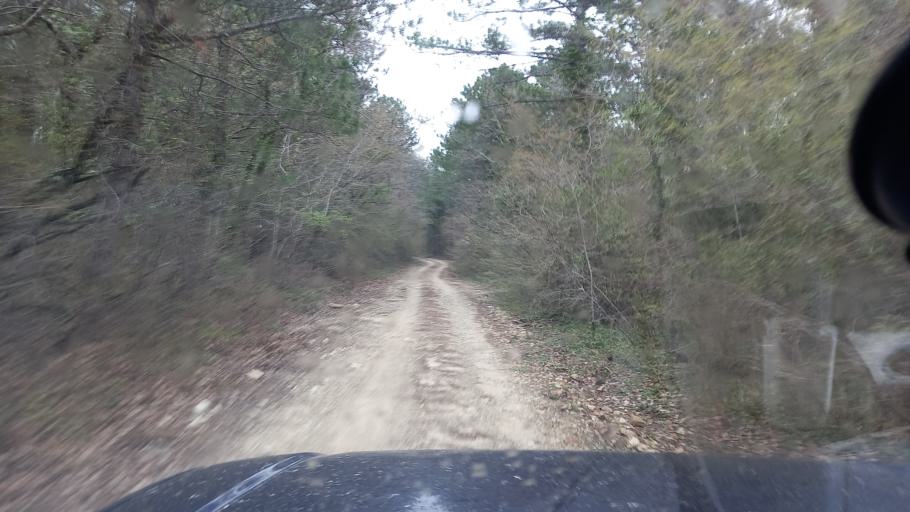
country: RU
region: Krasnodarskiy
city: Arkhipo-Osipovka
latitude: 44.3726
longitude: 38.4589
